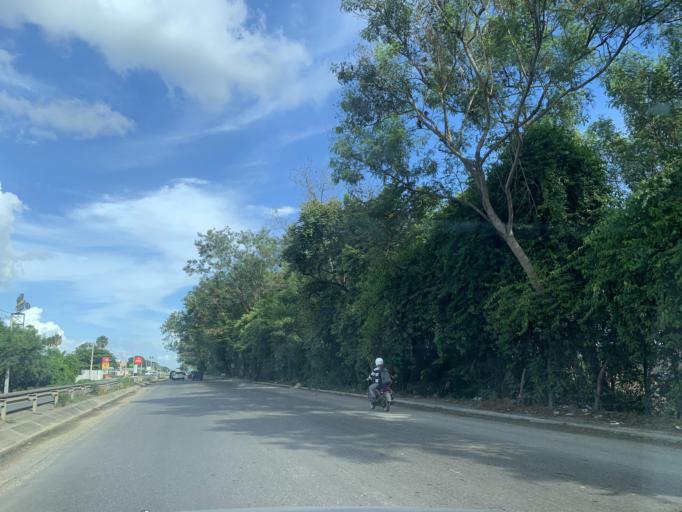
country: DO
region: Santiago
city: Villa Gonzalez
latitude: 19.5457
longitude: -70.8054
